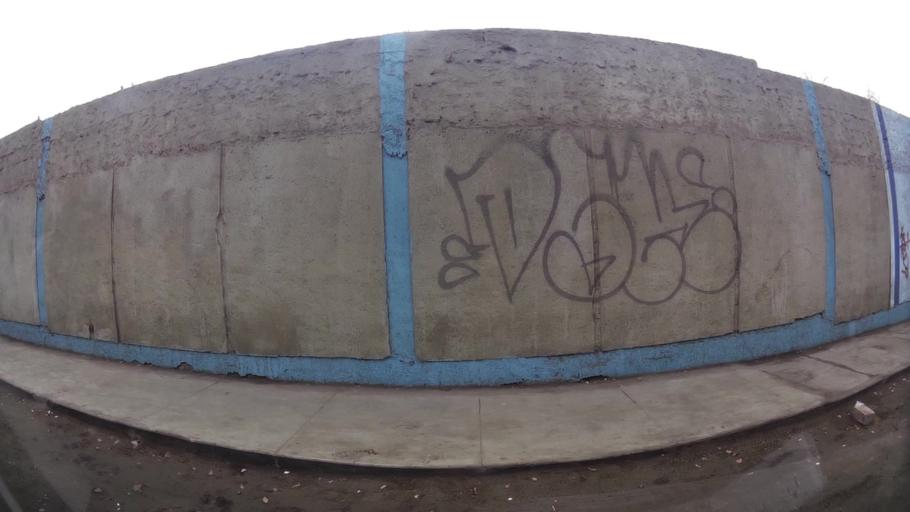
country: PE
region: Lima
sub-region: Lima
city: Surco
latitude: -12.1587
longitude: -76.9727
